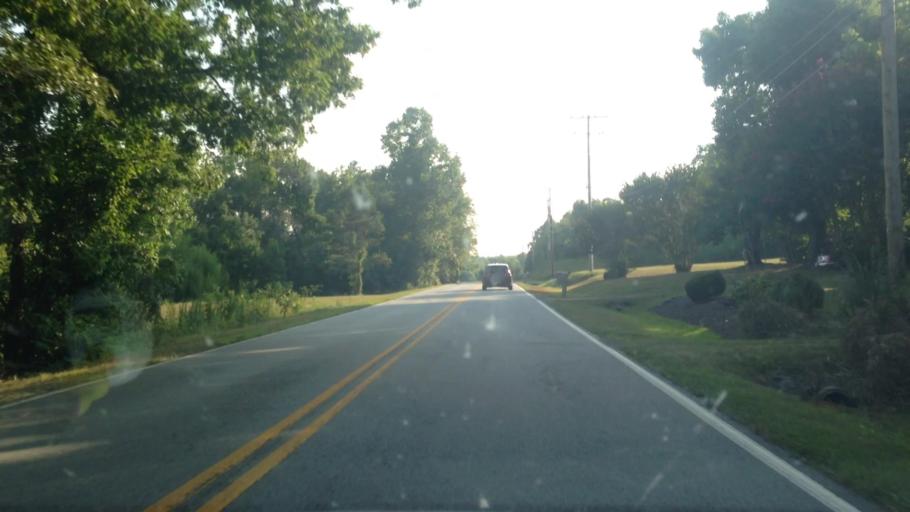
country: US
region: North Carolina
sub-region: Guilford County
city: High Point
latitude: 35.9502
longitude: -80.0722
